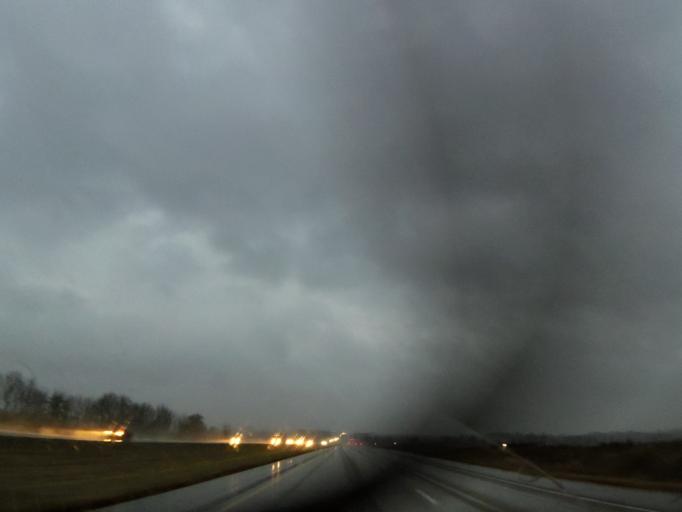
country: US
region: Iowa
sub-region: Worth County
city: Northwood
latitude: 43.3764
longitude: -93.3491
